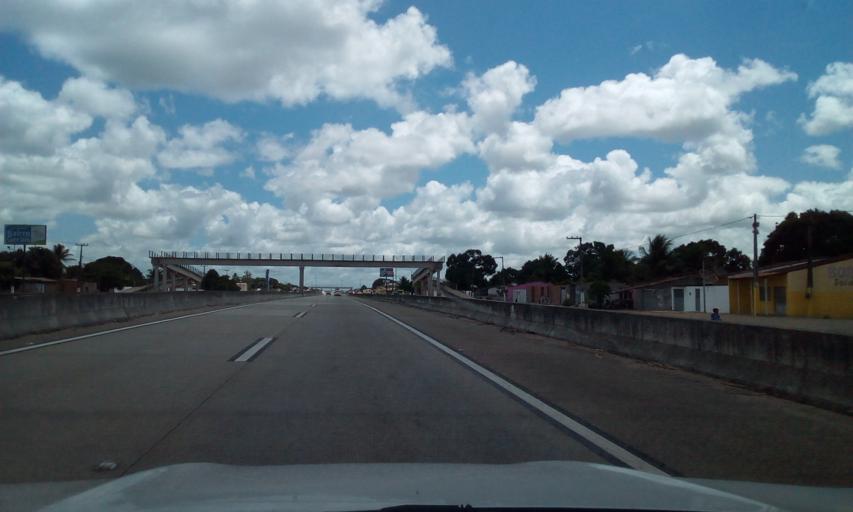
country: BR
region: Alagoas
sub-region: Junqueiro
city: Junqueiro
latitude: -9.8955
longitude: -36.3718
